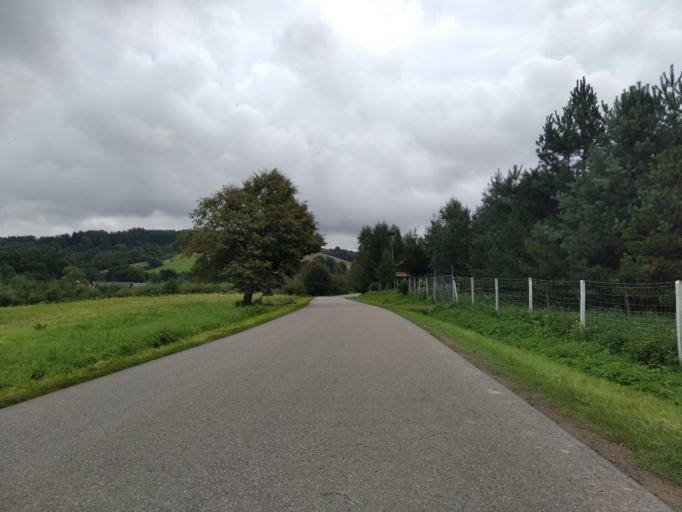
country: PL
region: Subcarpathian Voivodeship
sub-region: Powiat brzozowski
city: Nozdrzec
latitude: 49.7336
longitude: 22.2656
